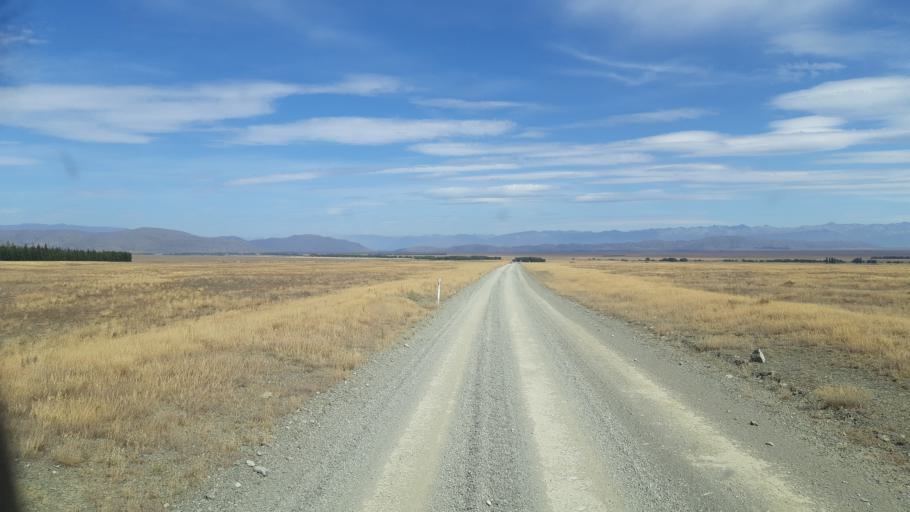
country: NZ
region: Canterbury
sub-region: Timaru District
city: Pleasant Point
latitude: -44.1949
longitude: 170.5453
